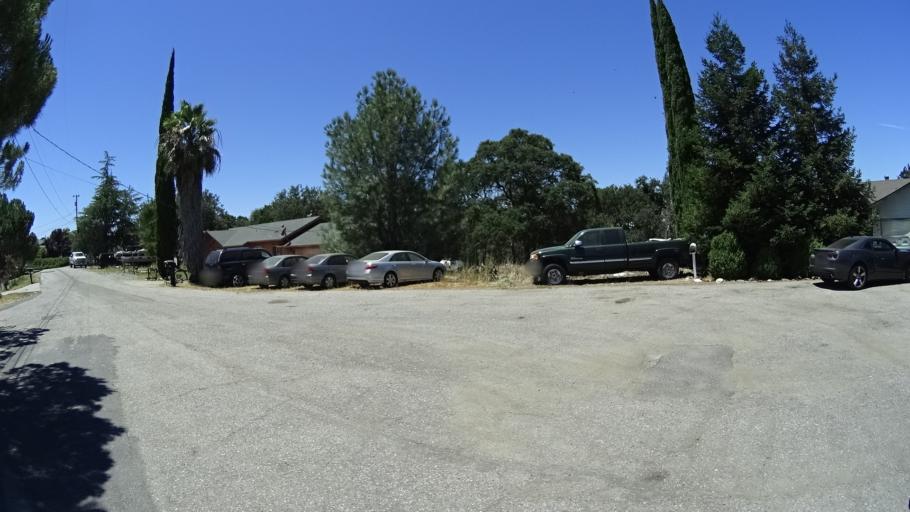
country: US
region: California
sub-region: Calaveras County
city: Rancho Calaveras
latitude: 38.1519
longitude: -120.8482
